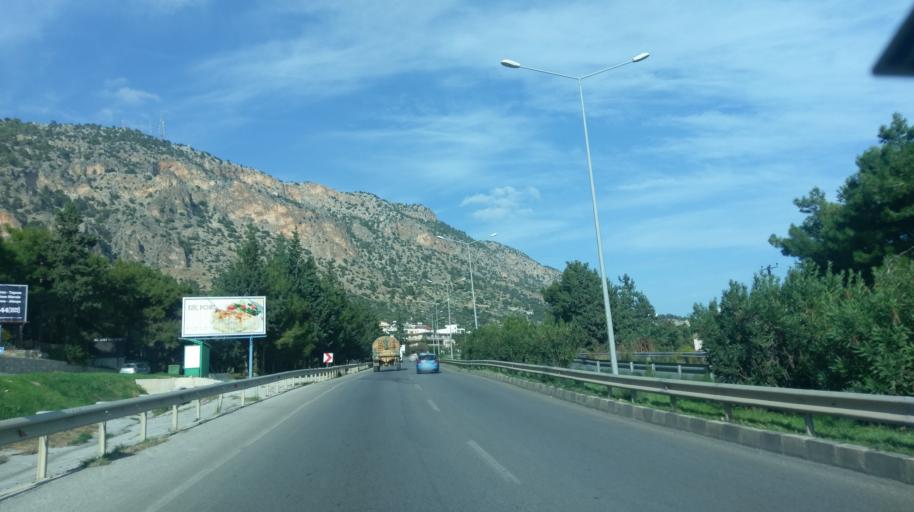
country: CY
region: Keryneia
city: Kyrenia
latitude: 35.2944
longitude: 33.2770
